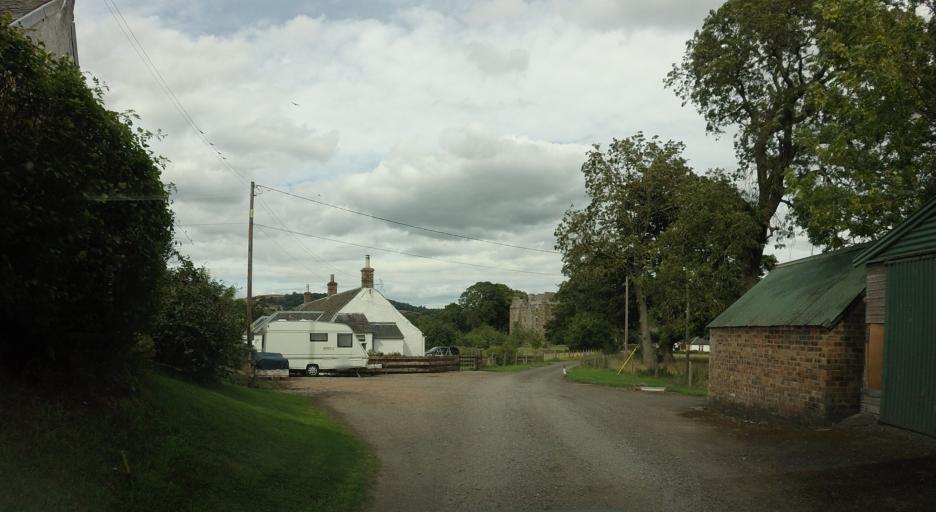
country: GB
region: Scotland
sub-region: Perth and Kinross
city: Bridge of Earn
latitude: 56.3733
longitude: -3.3565
